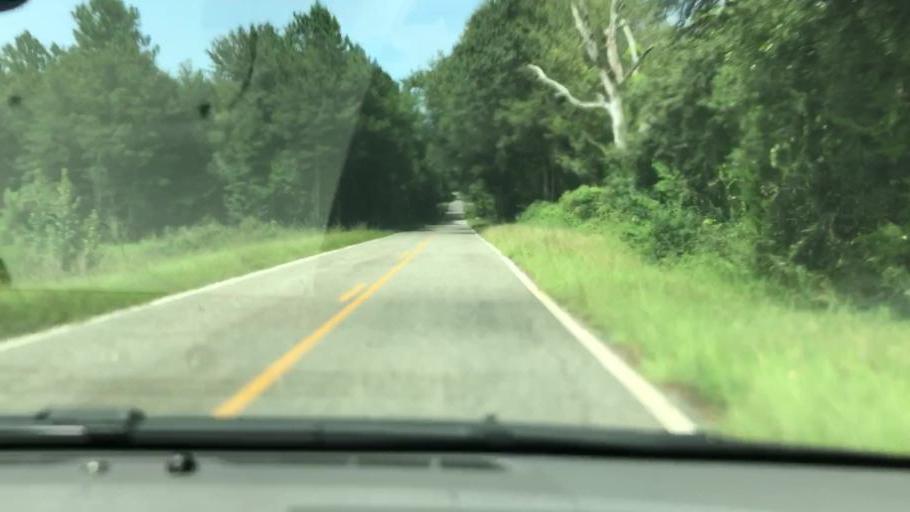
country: US
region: Georgia
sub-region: Seminole County
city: Donalsonville
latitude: 31.1502
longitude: -84.9949
